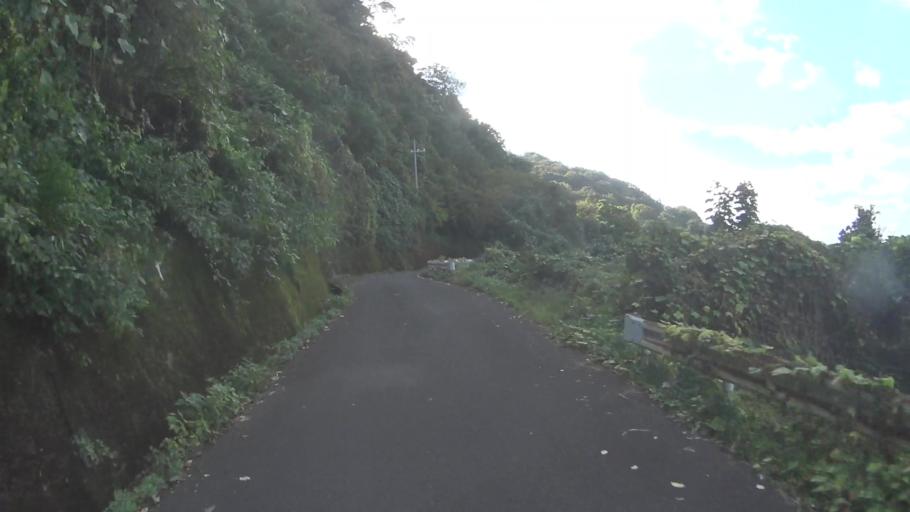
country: JP
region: Kyoto
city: Maizuru
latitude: 35.5679
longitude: 135.4178
